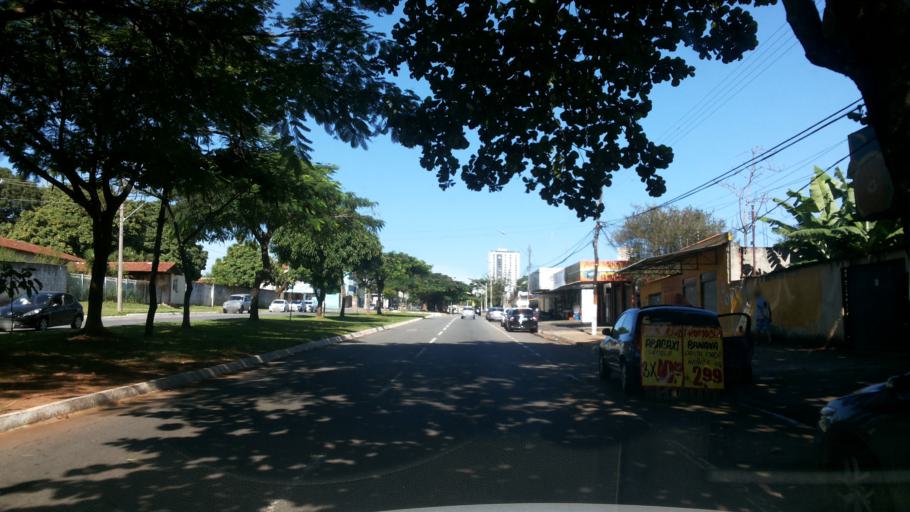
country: BR
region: Goias
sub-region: Goiania
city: Goiania
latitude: -16.7055
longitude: -49.2489
